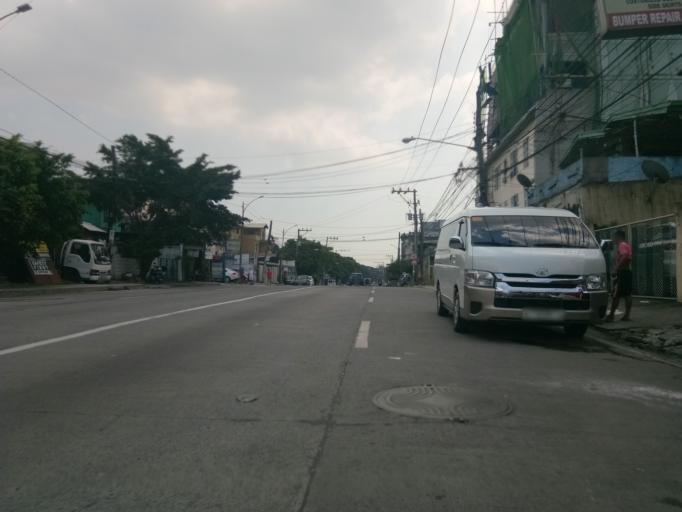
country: PH
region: Metro Manila
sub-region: Marikina
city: Calumpang
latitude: 14.6178
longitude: 121.0644
